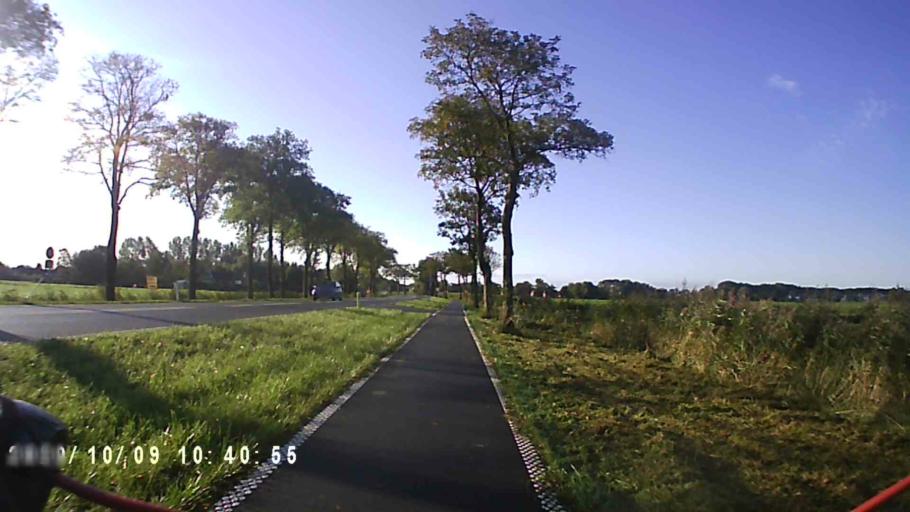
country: NL
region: Groningen
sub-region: Gemeente Winsum
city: Winsum
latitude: 53.2797
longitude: 6.5350
